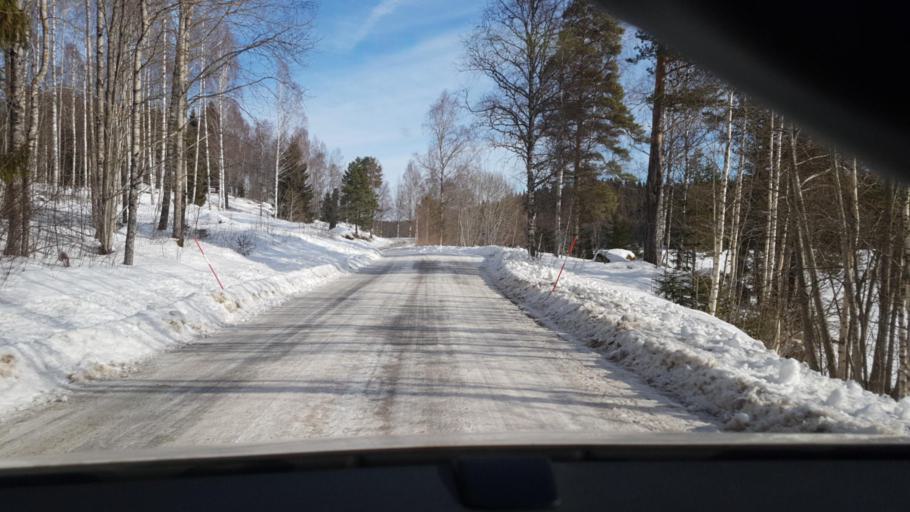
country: NO
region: Hedmark
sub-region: Eidskog
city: Skotterud
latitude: 59.8749
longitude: 11.9773
